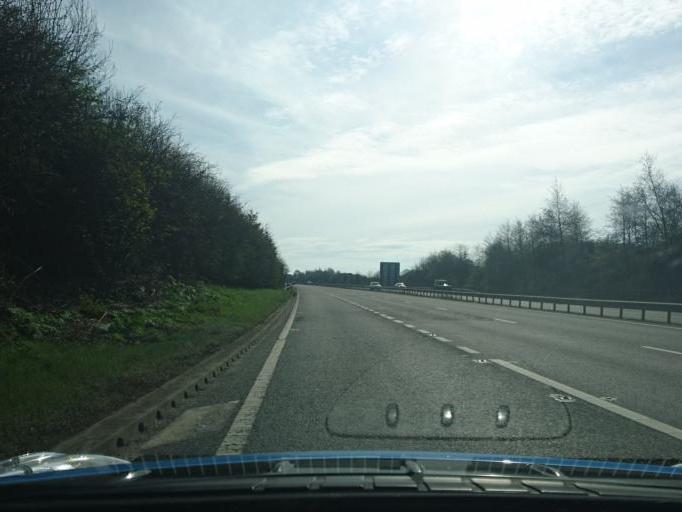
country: GB
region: England
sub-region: Herefordshire
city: Donnington
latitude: 51.9964
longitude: -2.3574
